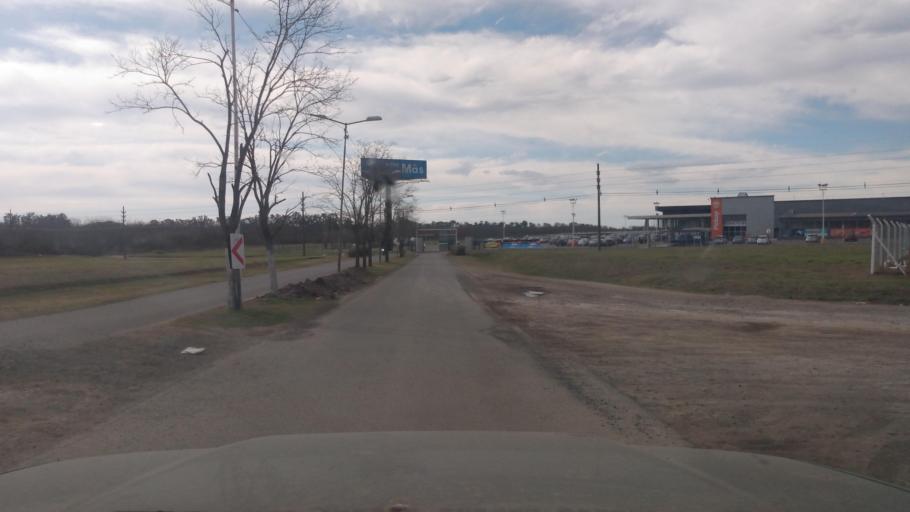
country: AR
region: Buenos Aires
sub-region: Partido de Lujan
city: Lujan
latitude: -34.5482
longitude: -59.1127
